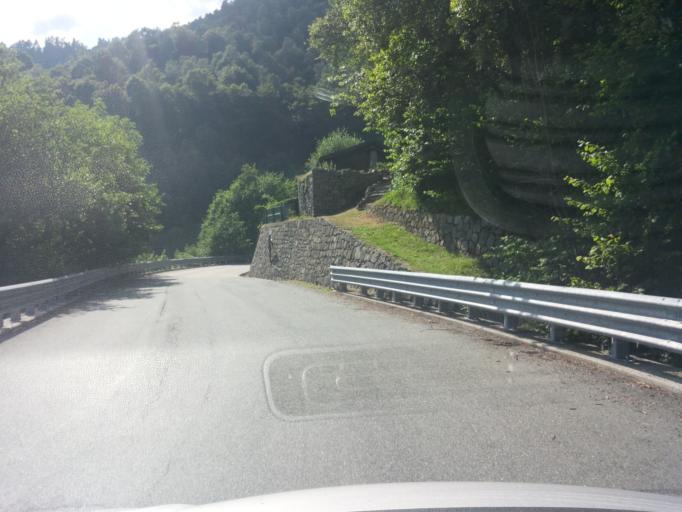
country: IT
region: Piedmont
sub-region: Provincia di Biella
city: Quittengo
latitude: 45.6656
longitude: 8.0261
